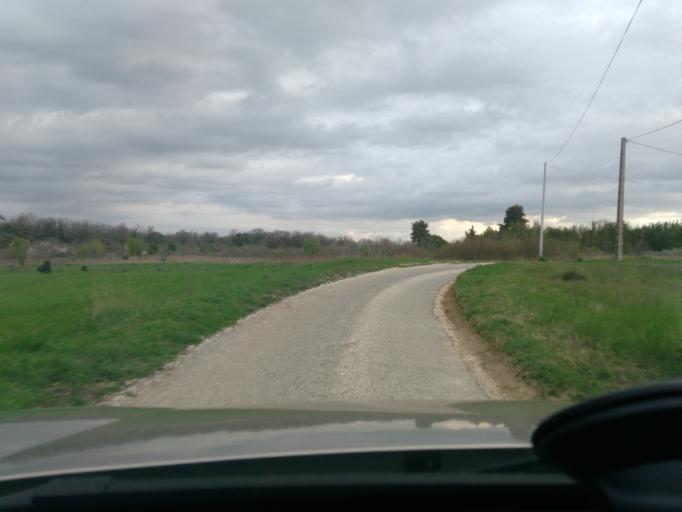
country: FR
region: Rhone-Alpes
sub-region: Departement de la Drome
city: Montboucher-sur-Jabron
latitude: 44.5569
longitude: 4.7856
